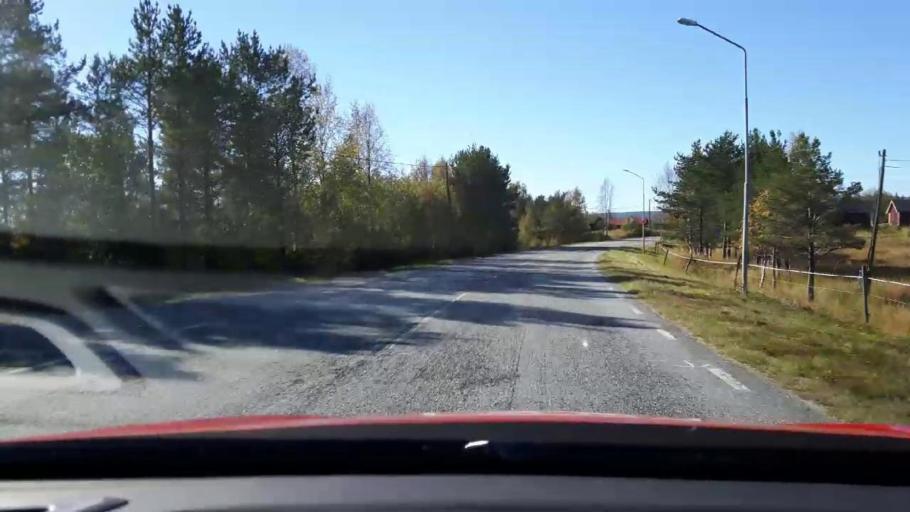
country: SE
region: Jaemtland
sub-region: Harjedalens Kommun
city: Sveg
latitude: 62.3209
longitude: 14.0606
